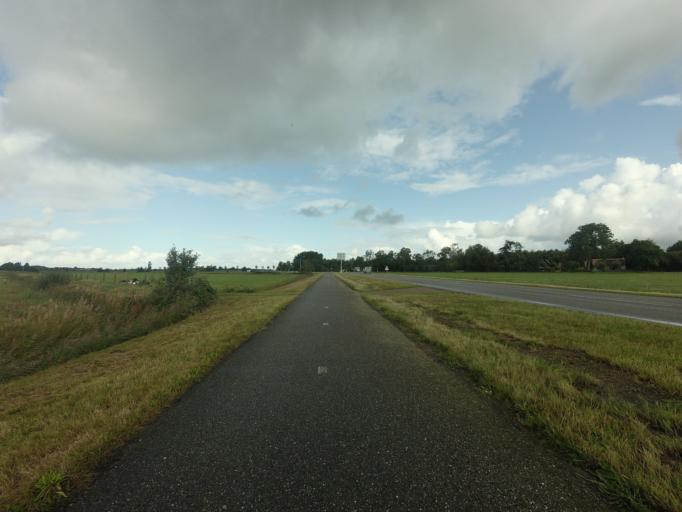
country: NL
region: Friesland
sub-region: Gemeente Tytsjerksteradiel
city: Garyp
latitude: 53.1588
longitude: 5.9503
